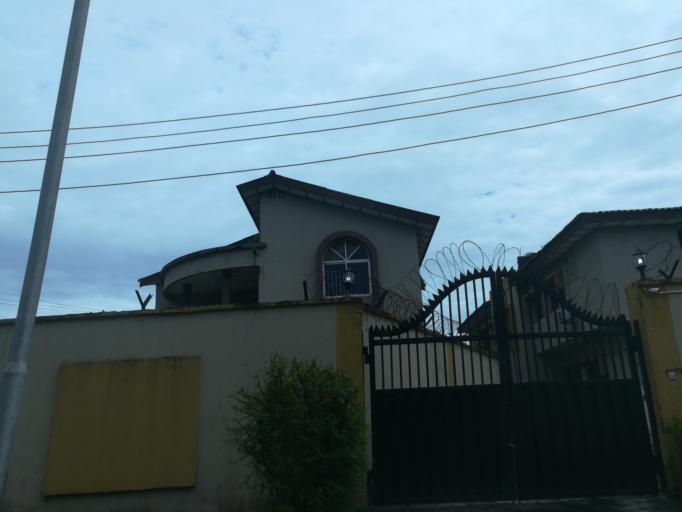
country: NG
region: Lagos
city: Ikoyi
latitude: 6.4401
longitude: 3.4775
